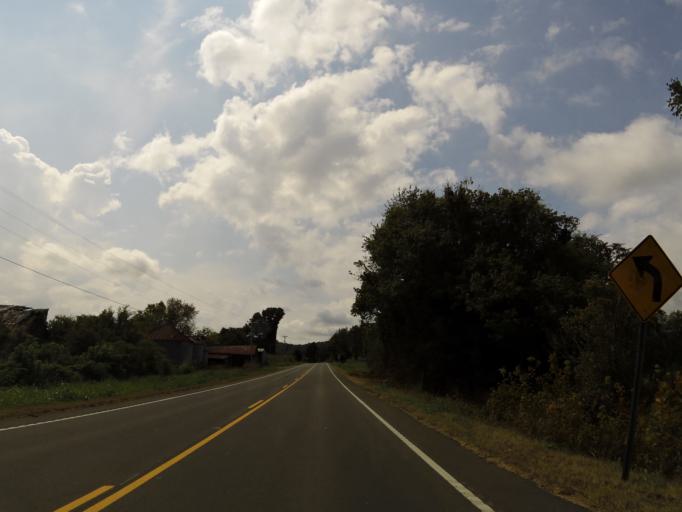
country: US
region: Tennessee
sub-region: Perry County
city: Linden
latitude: 35.7413
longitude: -87.8103
